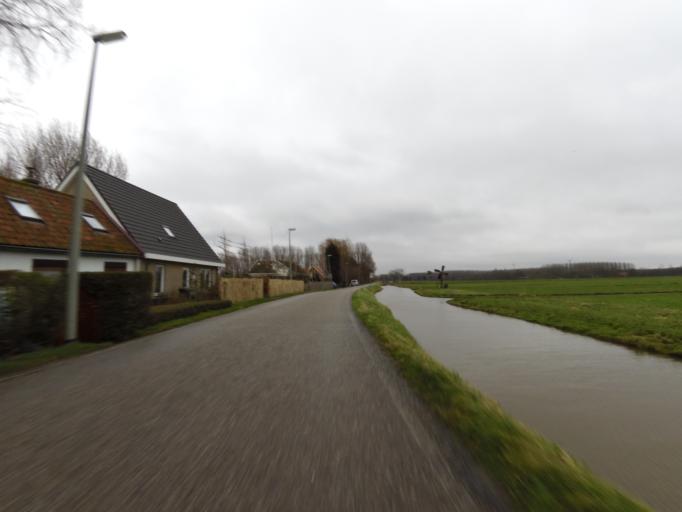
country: NL
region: South Holland
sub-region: Gemeente Maassluis
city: Maassluis
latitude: 51.9164
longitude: 4.2880
